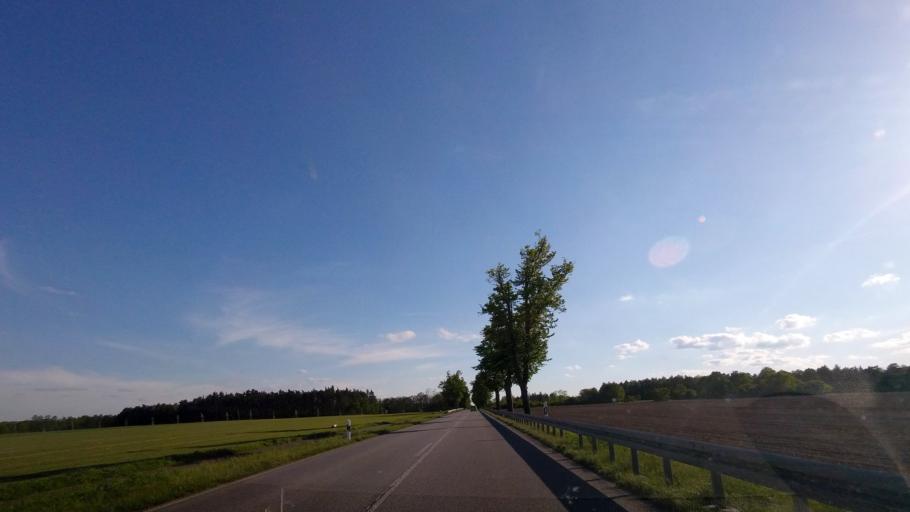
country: DE
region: Brandenburg
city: Luebben
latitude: 51.9230
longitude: 13.8745
